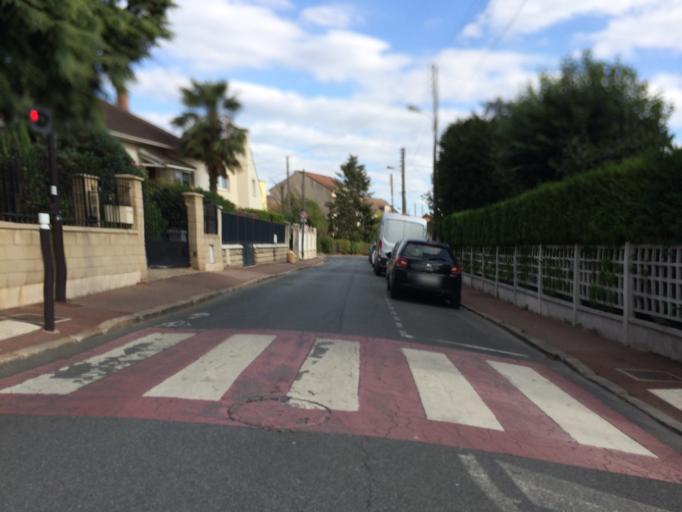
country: FR
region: Ile-de-France
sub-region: Departement de l'Essonne
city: Chilly-Mazarin
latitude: 48.7071
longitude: 2.3232
